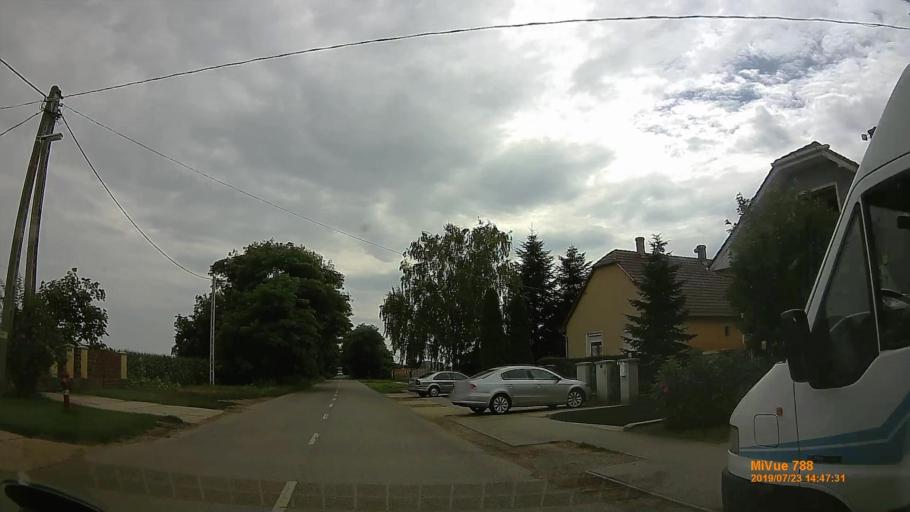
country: HU
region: Szabolcs-Szatmar-Bereg
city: Nyiregyhaza
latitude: 47.9106
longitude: 21.6744
